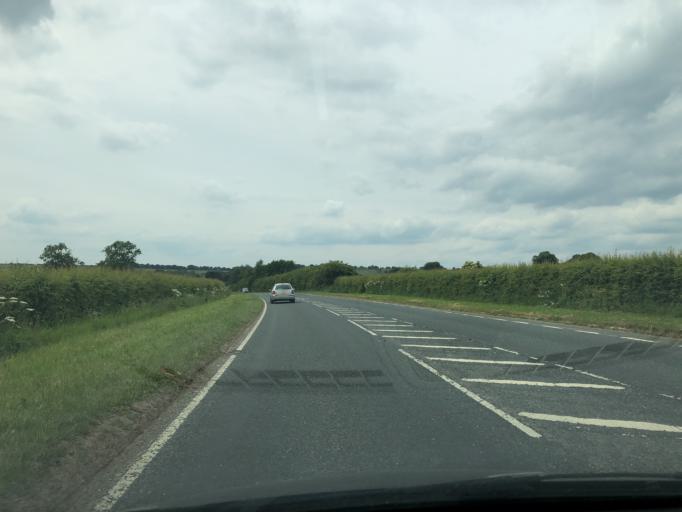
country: GB
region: England
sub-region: North Yorkshire
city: Pickering
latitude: 54.2624
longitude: -0.8166
